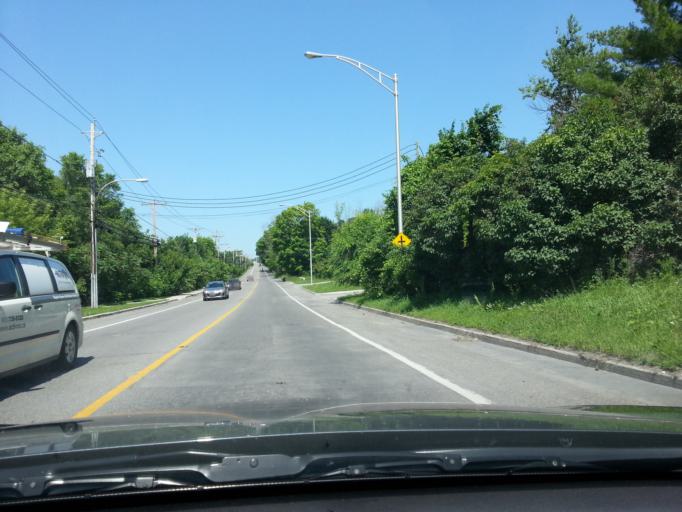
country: CA
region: Ontario
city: Bells Corners
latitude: 45.4022
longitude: -75.8557
